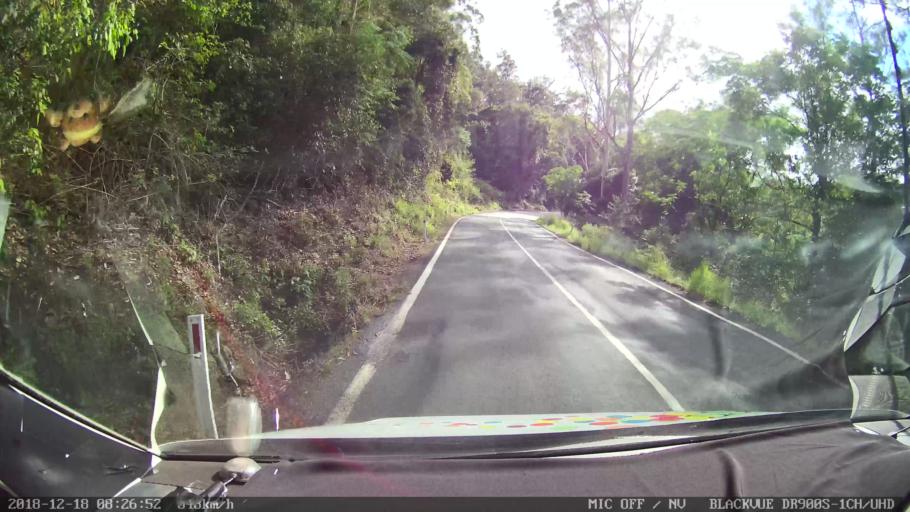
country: AU
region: New South Wales
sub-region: Kyogle
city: Kyogle
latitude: -28.3260
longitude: 152.7456
